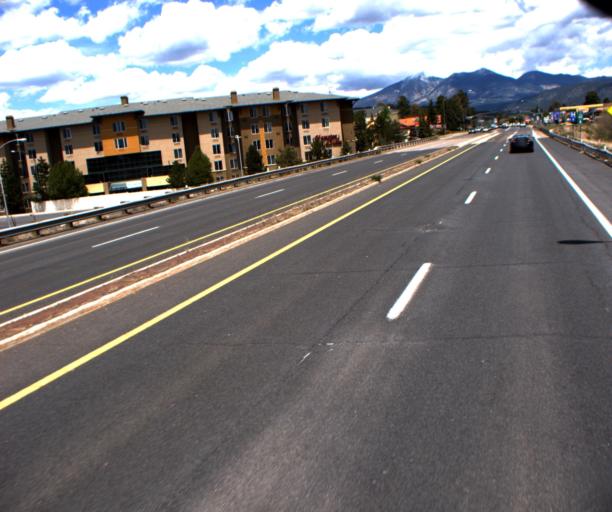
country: US
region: Arizona
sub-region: Coconino County
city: Flagstaff
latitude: 35.1766
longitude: -111.6614
